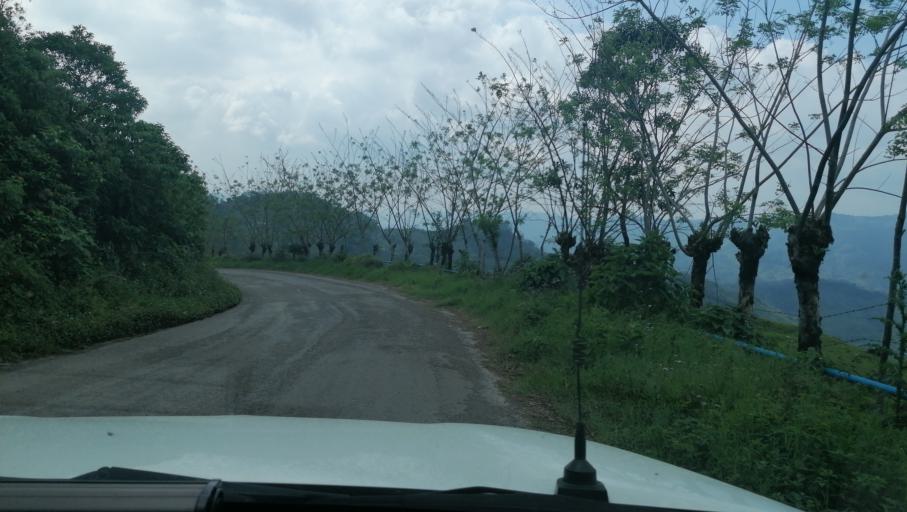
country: MX
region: Chiapas
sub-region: Francisco Leon
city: San Miguel la Sardina
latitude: 17.2372
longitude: -93.3069
